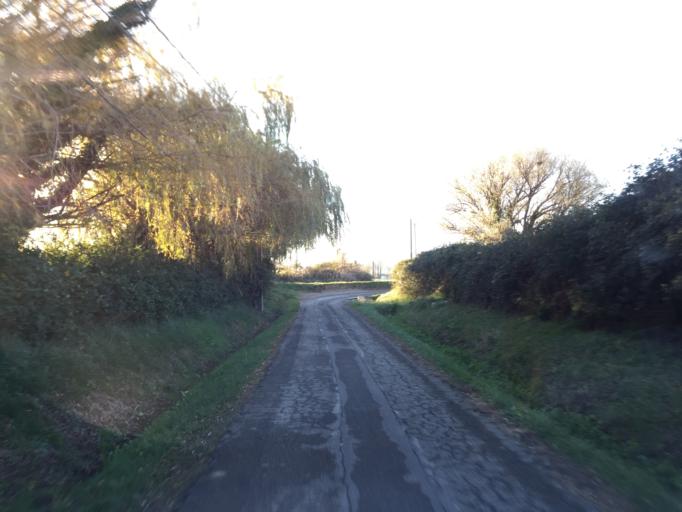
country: FR
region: Provence-Alpes-Cote d'Azur
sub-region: Departement du Vaucluse
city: Bedarrides
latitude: 44.0504
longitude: 4.8936
